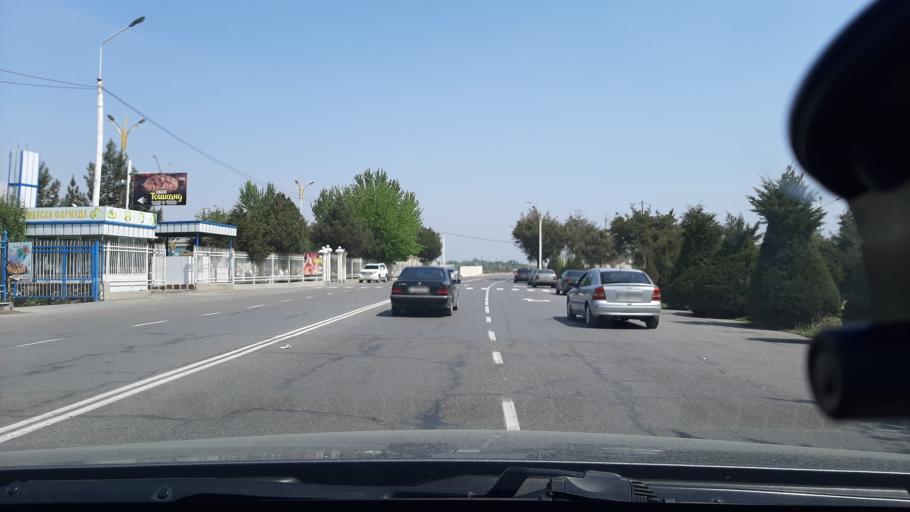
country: TJ
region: Viloyati Sughd
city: Khujand
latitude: 40.2912
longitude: 69.6256
